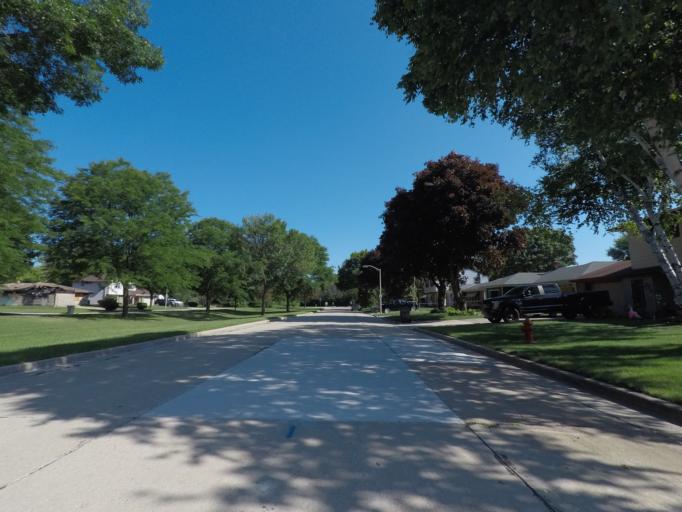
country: US
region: Wisconsin
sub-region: Waukesha County
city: Elm Grove
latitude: 43.0227
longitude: -88.0619
